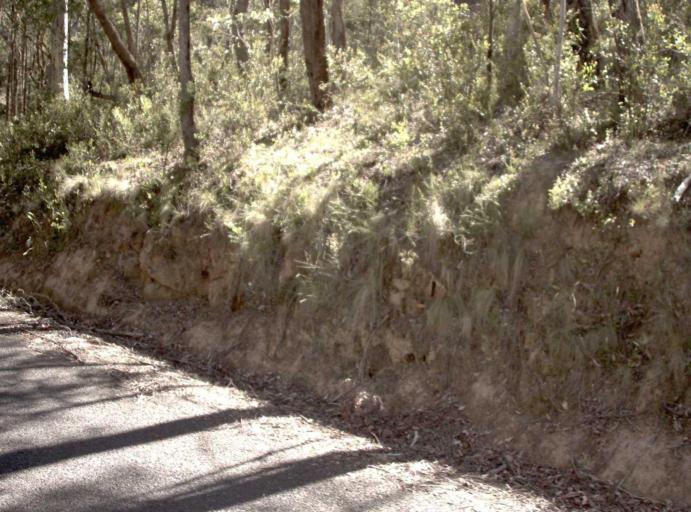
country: AU
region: New South Wales
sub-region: Bombala
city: Bombala
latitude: -37.1477
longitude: 148.7243
